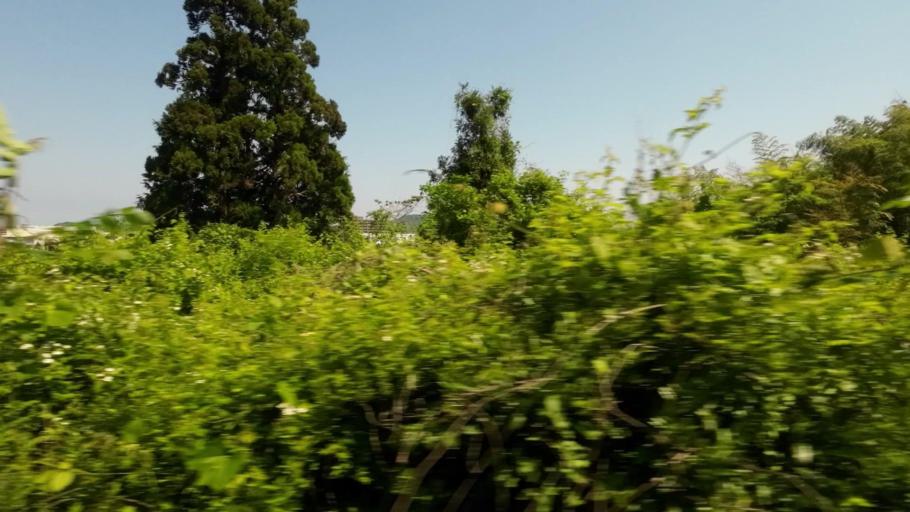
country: JP
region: Ehime
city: Niihama
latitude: 33.9724
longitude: 133.3504
